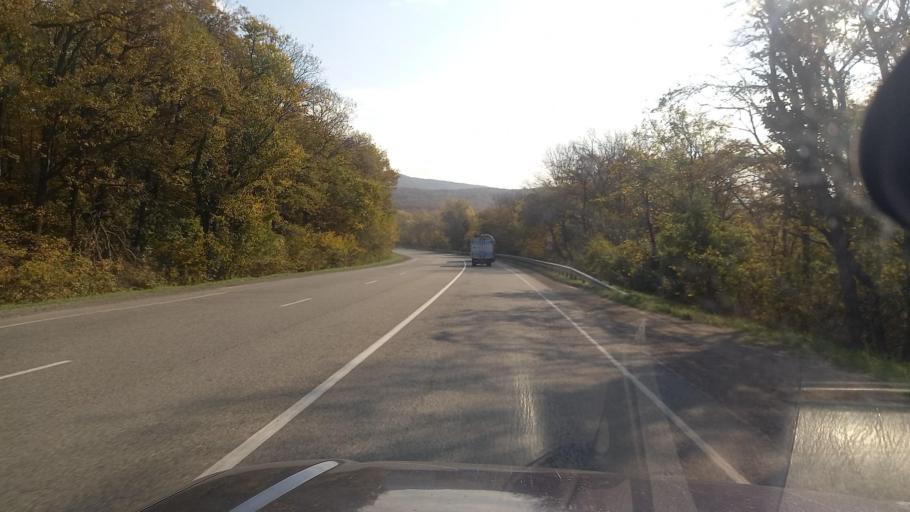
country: RU
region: Krasnodarskiy
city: Verkhnebakanskiy
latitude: 44.8417
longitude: 37.7041
